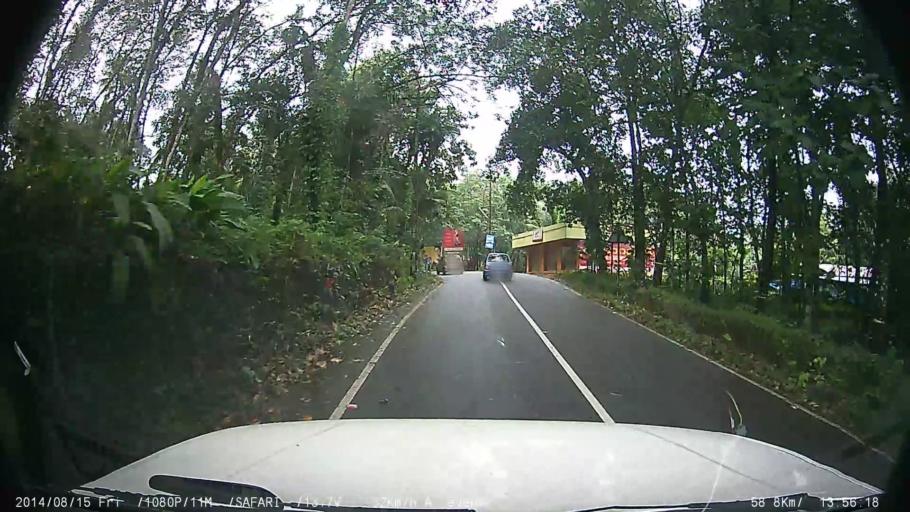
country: IN
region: Kerala
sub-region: Kottayam
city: Lalam
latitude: 9.7182
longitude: 76.6612
